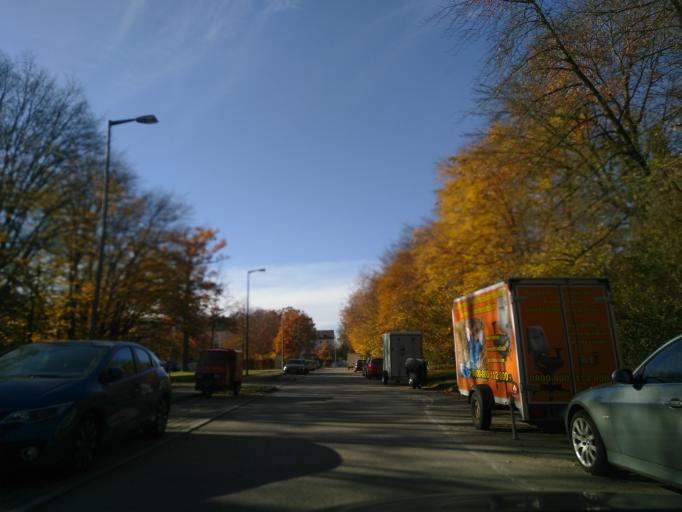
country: DE
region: Bavaria
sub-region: Upper Bavaria
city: Unterhaching
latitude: 48.0956
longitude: 11.5940
